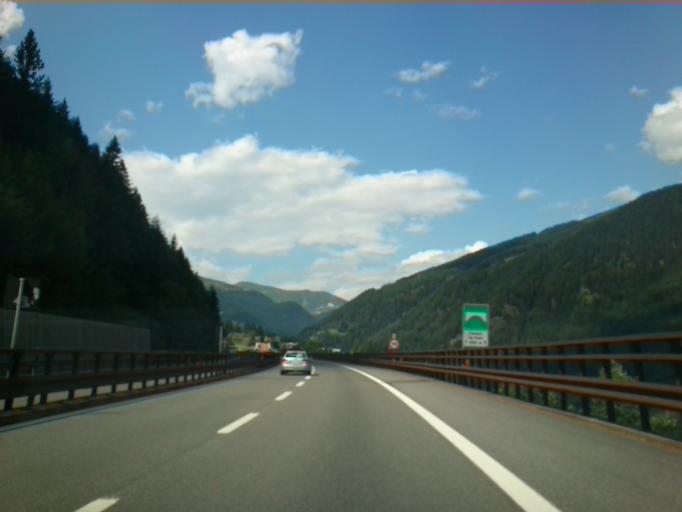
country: IT
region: Trentino-Alto Adige
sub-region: Bolzano
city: Brennero - Brenner
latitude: 46.9193
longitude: 11.4423
